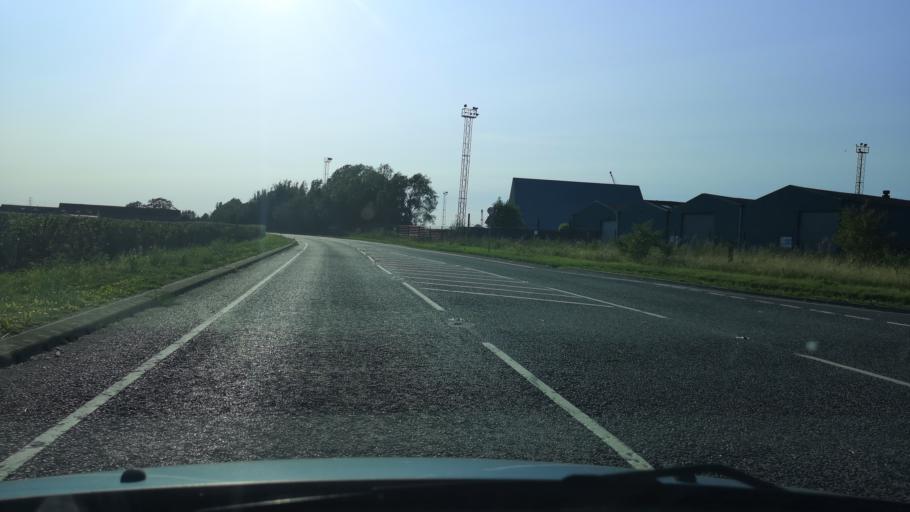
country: GB
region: England
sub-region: North Lincolnshire
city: Gunness
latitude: 53.6062
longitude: -0.7044
